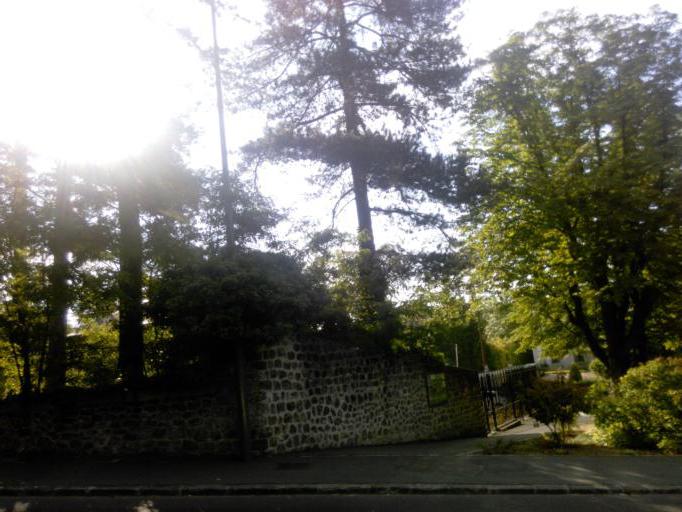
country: FR
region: Ile-de-France
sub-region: Departement des Yvelines
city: Viroflay
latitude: 48.8114
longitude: 2.1509
